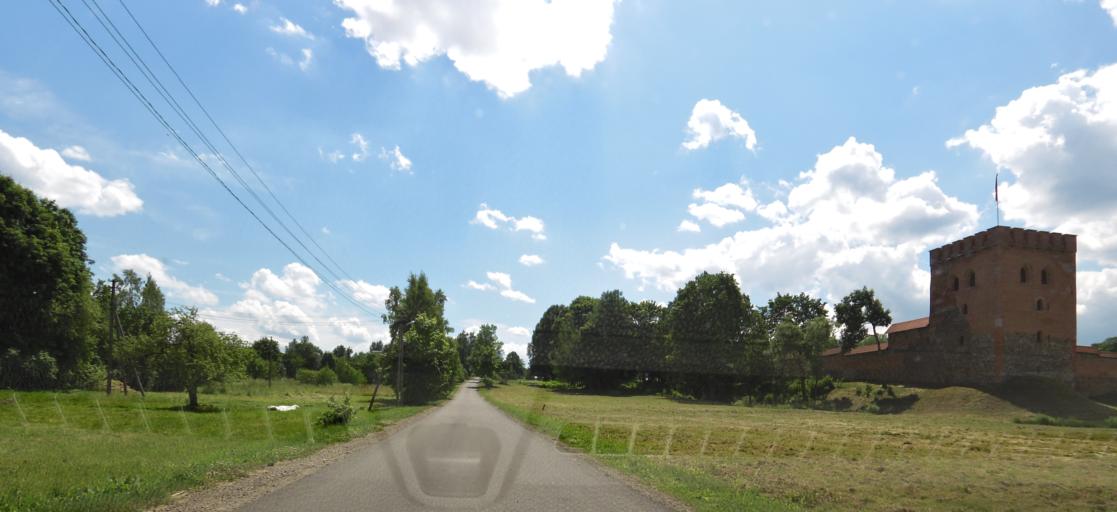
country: LT
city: Skaidiskes
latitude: 54.5408
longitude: 25.6525
